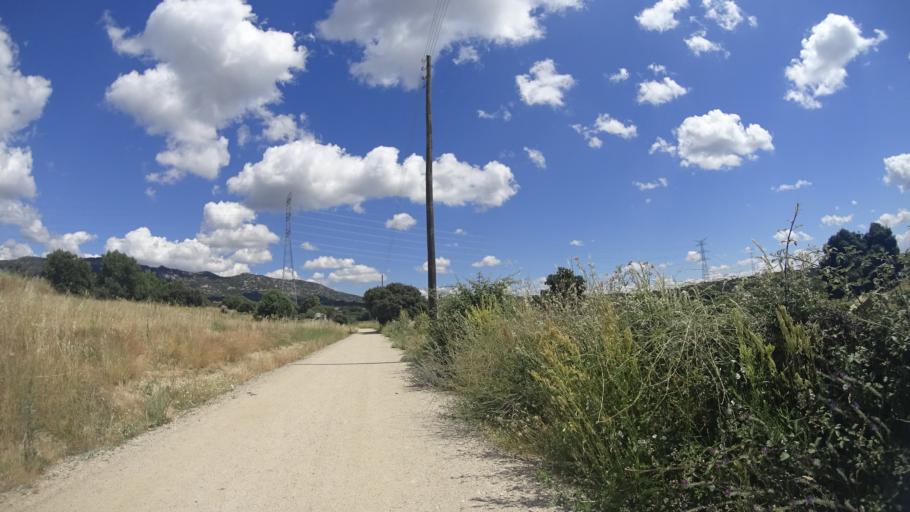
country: ES
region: Madrid
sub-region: Provincia de Madrid
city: Hoyo de Manzanares
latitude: 40.6106
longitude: -3.9033
